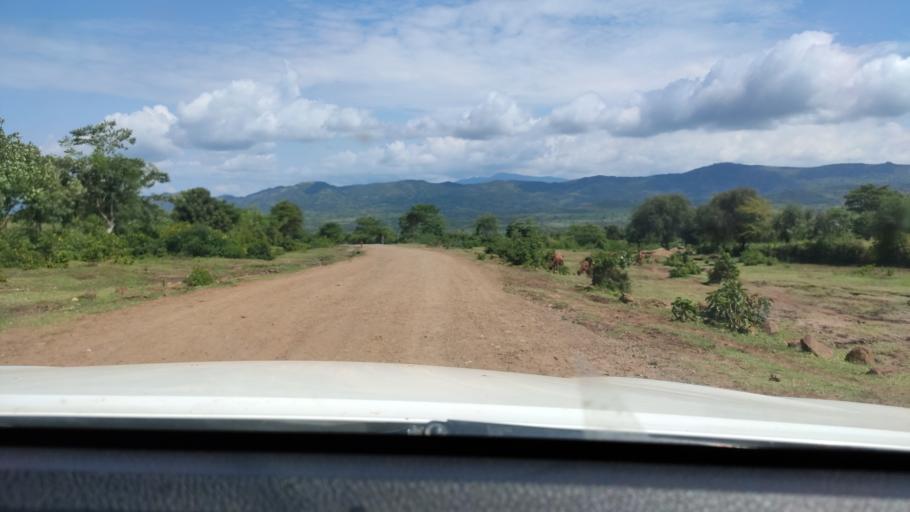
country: ET
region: Southern Nations, Nationalities, and People's Region
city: Felege Neway
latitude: 6.3655
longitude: 36.9835
